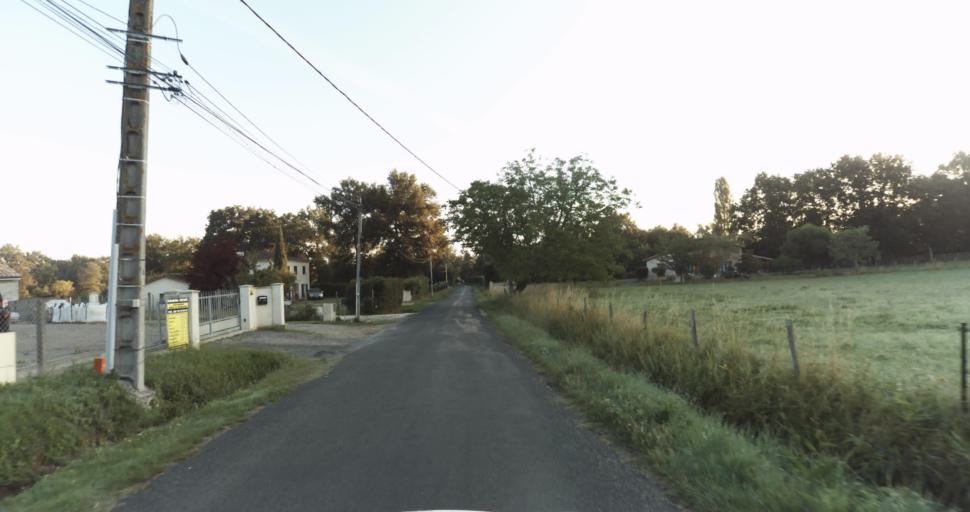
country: FR
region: Aquitaine
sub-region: Departement de la Gironde
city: Bazas
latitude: 44.4213
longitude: -0.2068
